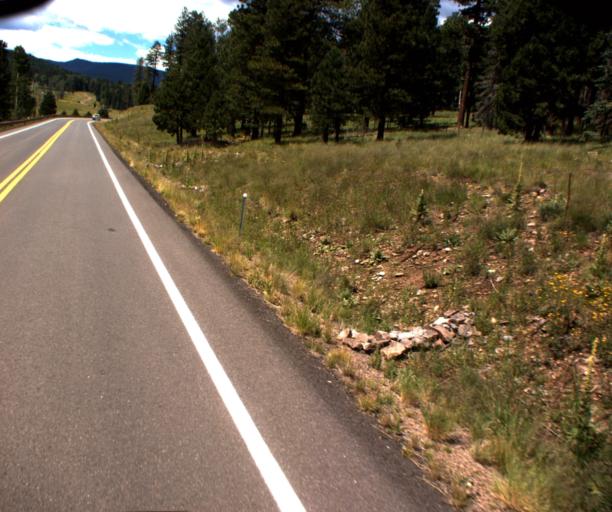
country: US
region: Arizona
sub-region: Apache County
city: Eagar
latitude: 33.9297
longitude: -109.4734
